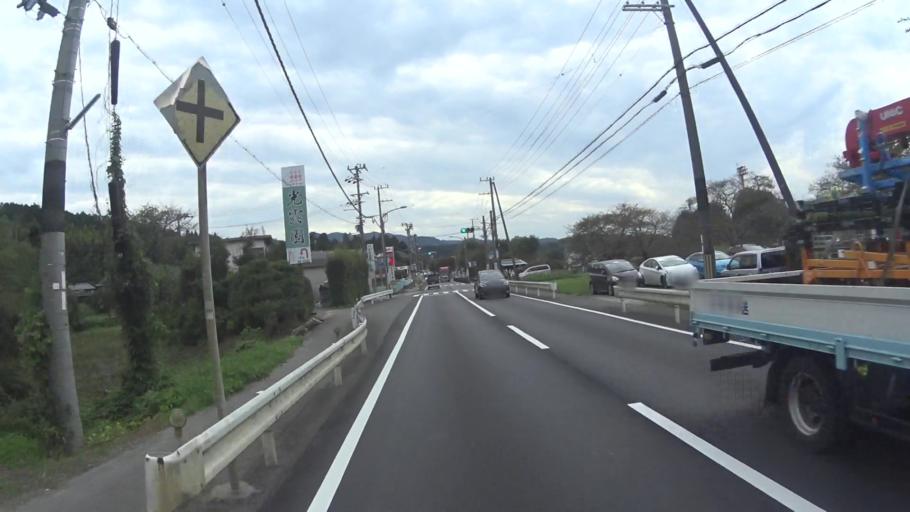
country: JP
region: Kyoto
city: Uji
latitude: 34.8565
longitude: 135.8673
